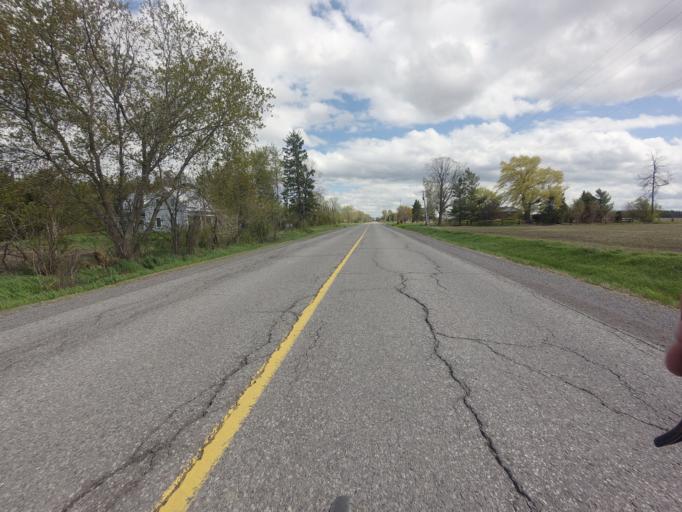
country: CA
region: Ontario
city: Carleton Place
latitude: 45.3515
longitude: -76.1139
